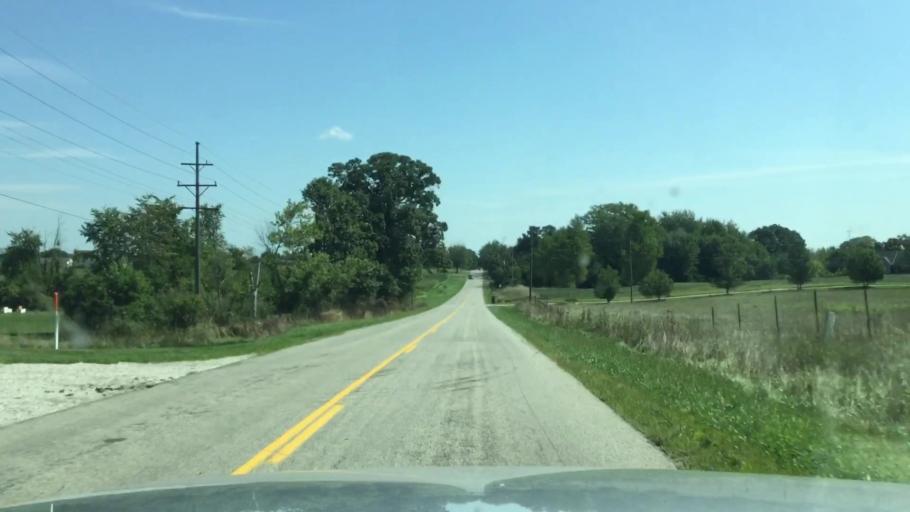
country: US
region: Michigan
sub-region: Lenawee County
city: Clinton
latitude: 42.0654
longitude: -83.9415
